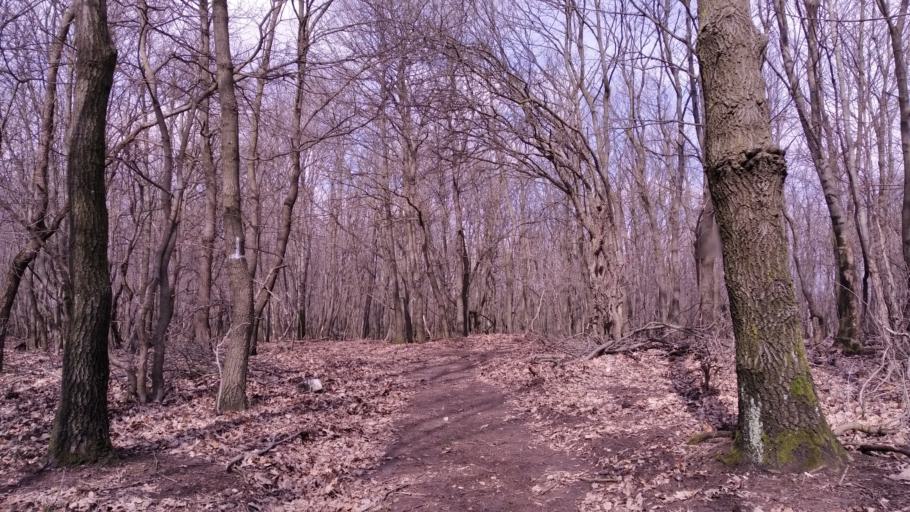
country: HU
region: Komarom-Esztergom
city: Oroszlany
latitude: 47.4015
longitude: 18.3406
